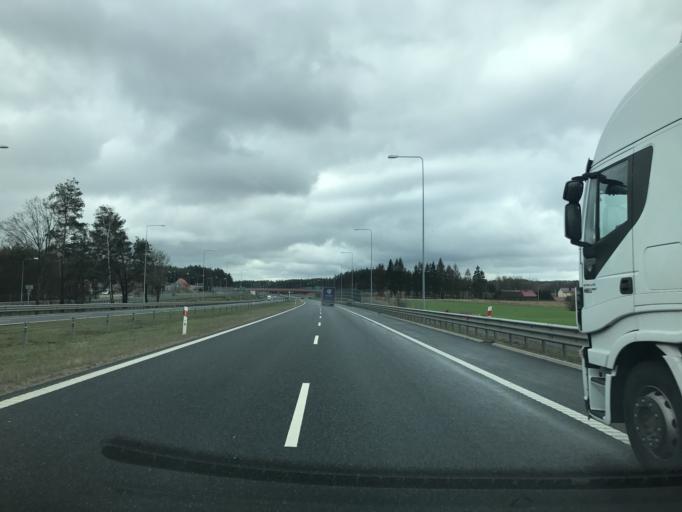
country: PL
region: Warmian-Masurian Voivodeship
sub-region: Powiat olsztynski
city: Olsztynek
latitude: 53.5372
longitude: 20.2736
